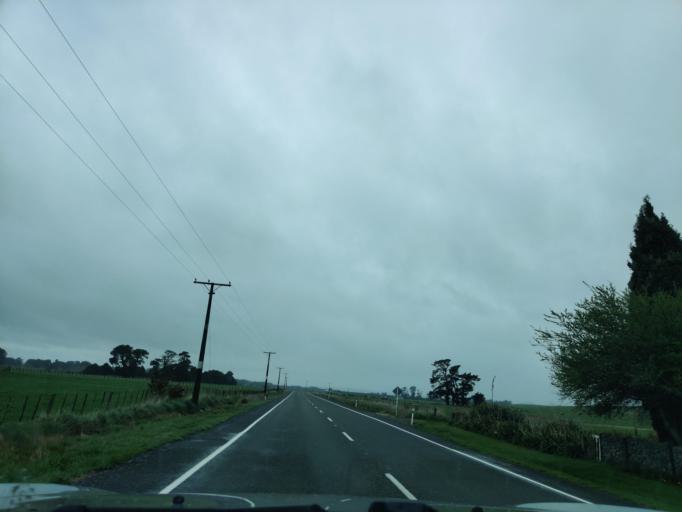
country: NZ
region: Hawke's Bay
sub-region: Hastings District
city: Hastings
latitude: -40.0203
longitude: 176.2715
